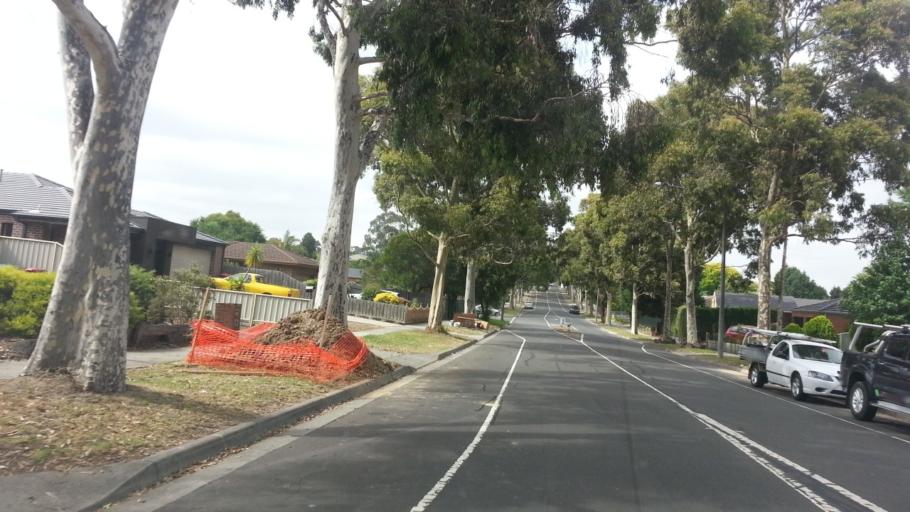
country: AU
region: Victoria
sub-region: Knox
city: Scoresby
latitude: -37.9155
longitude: 145.2463
